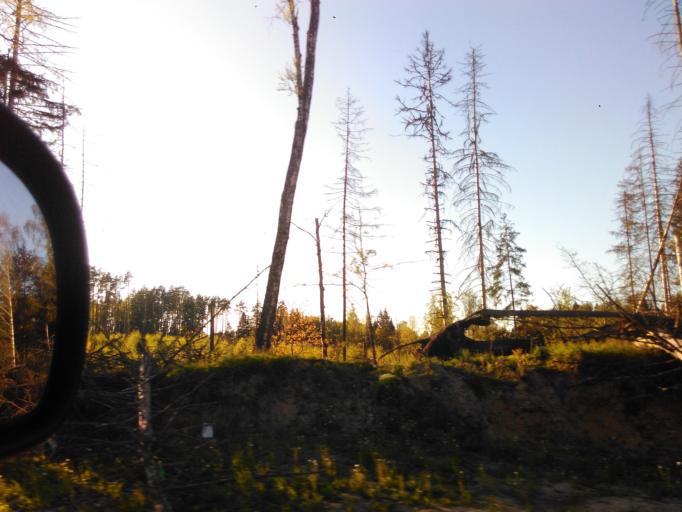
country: RU
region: Moskovskaya
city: Radumlya
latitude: 56.0474
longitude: 37.1120
